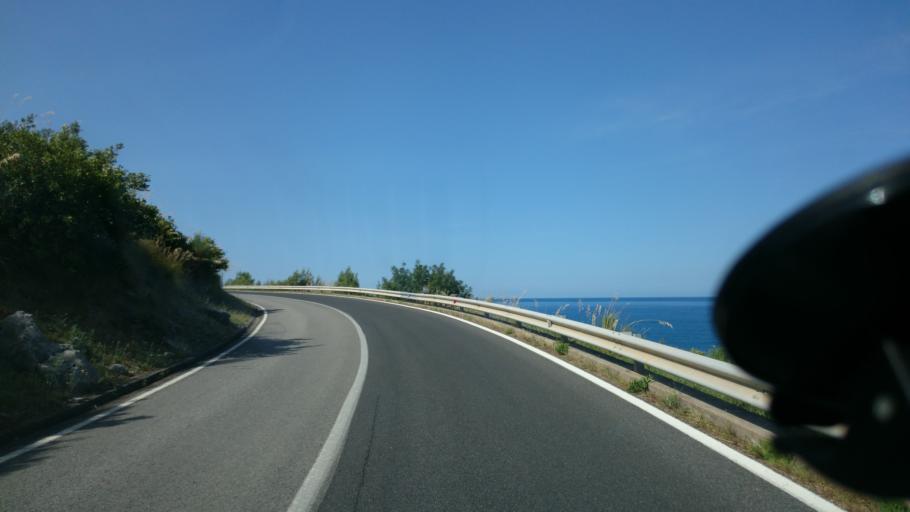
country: IT
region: Campania
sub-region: Provincia di Salerno
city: Sapri
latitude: 40.0630
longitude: 15.6285
